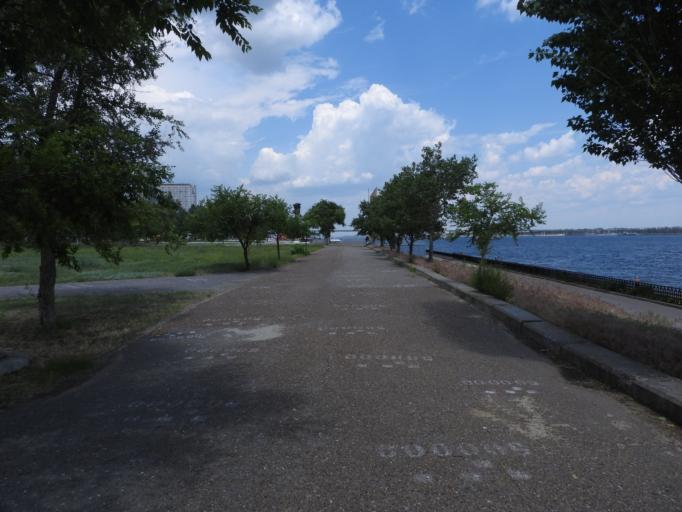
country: RU
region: Volgograd
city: Volgograd
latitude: 48.7107
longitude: 44.5327
